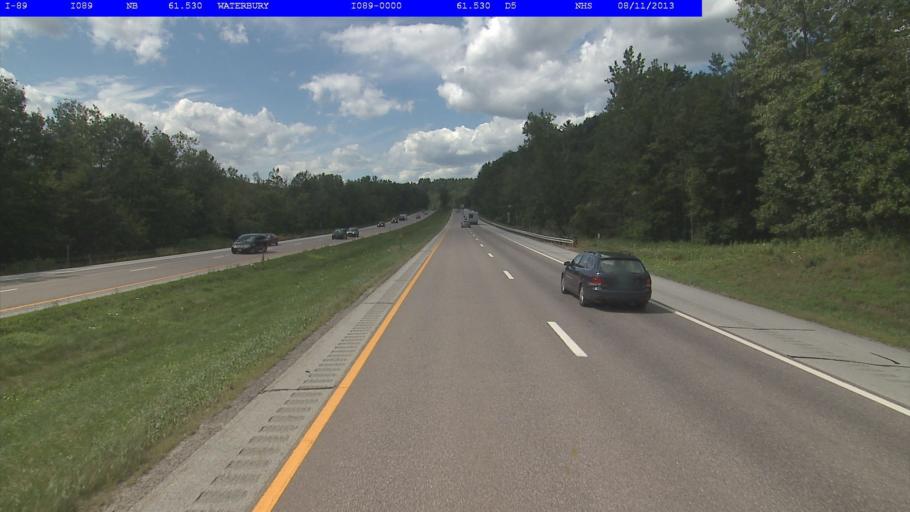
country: US
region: Vermont
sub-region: Washington County
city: Waterbury
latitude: 44.3191
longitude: -72.7261
